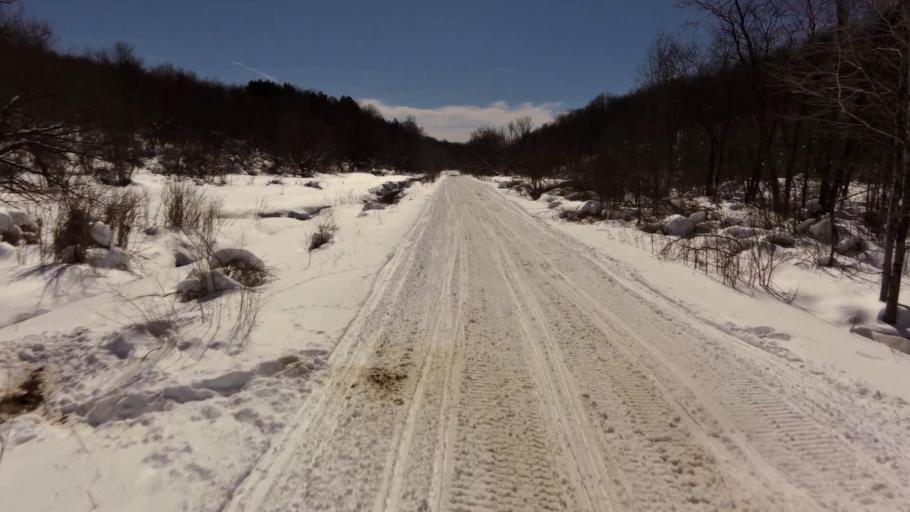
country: US
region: New York
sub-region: Cattaraugus County
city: Delevan
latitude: 42.4217
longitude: -78.4573
